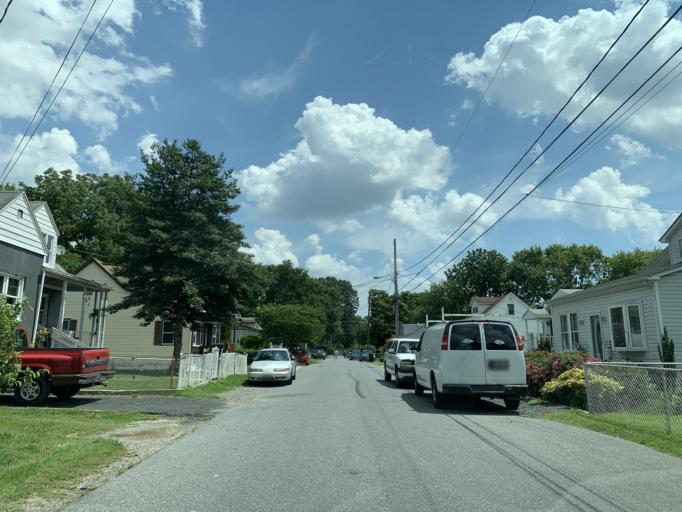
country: US
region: Maryland
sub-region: Baltimore County
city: Essex
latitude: 39.3084
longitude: -76.4662
